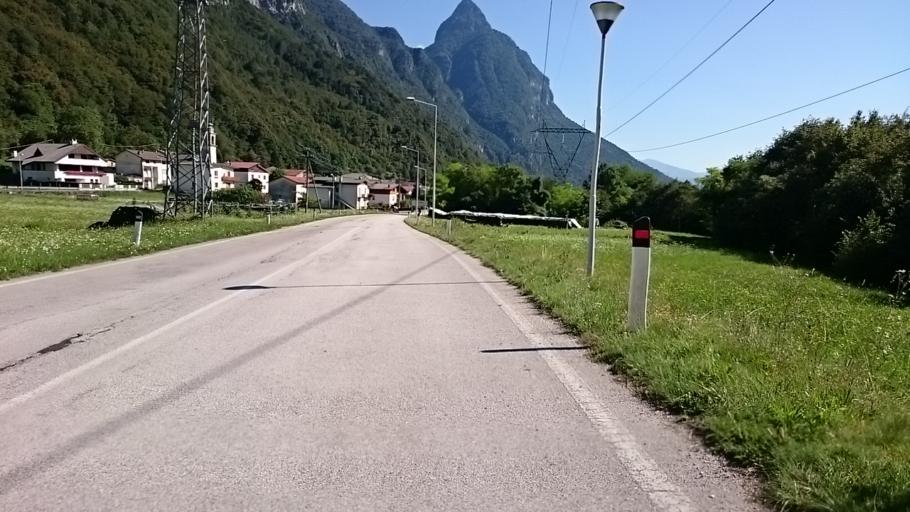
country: IT
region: Veneto
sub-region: Provincia di Belluno
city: Longarone
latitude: 46.2622
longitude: 12.3123
